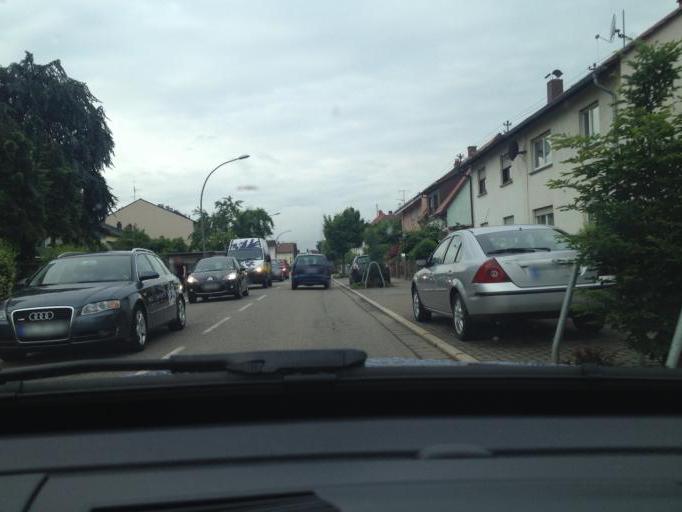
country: DE
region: Baden-Wuerttemberg
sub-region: Karlsruhe Region
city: Oftersheim
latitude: 49.3738
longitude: 8.5892
